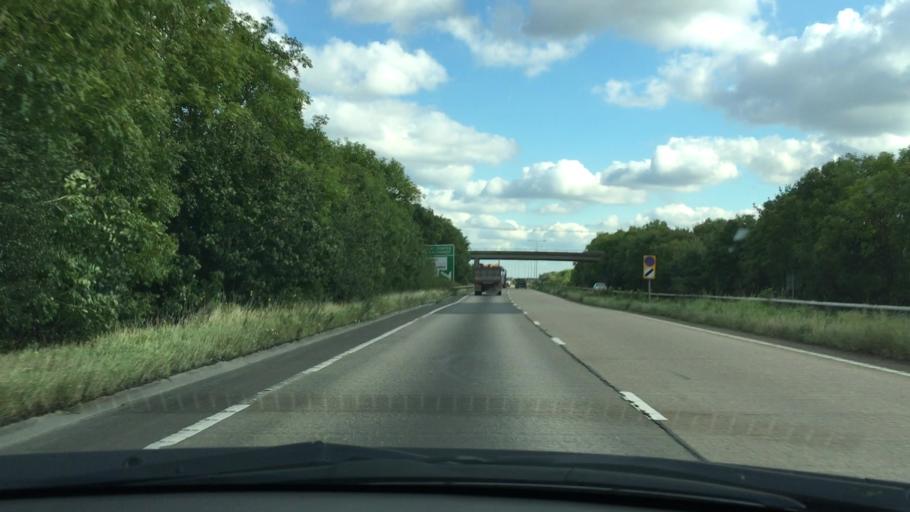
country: GB
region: England
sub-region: North East Lincolnshire
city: Healing
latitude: 53.5895
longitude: -0.1593
